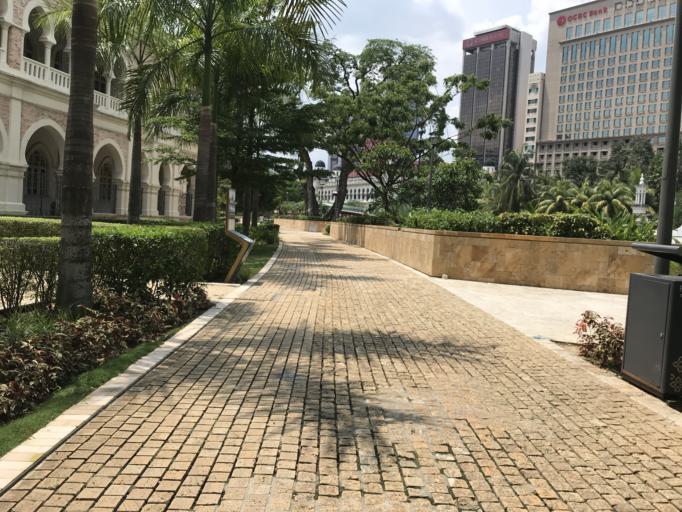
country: MY
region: Kuala Lumpur
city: Kuala Lumpur
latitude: 3.1480
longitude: 101.6951
